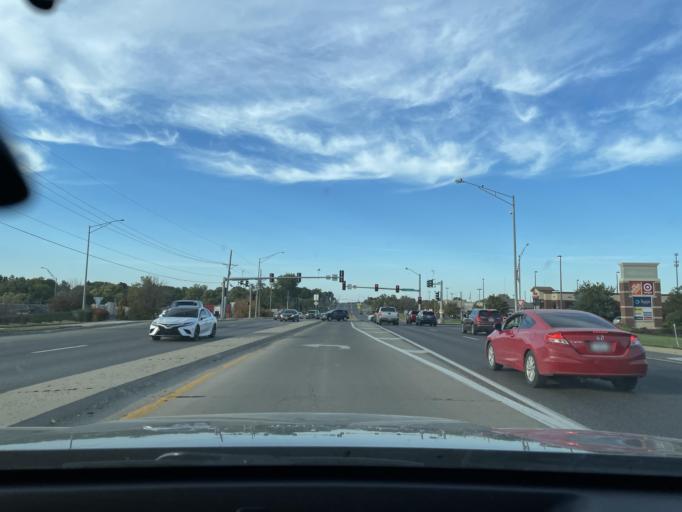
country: US
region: Missouri
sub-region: Andrew County
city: Country Club Village
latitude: 39.8132
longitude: -94.8151
